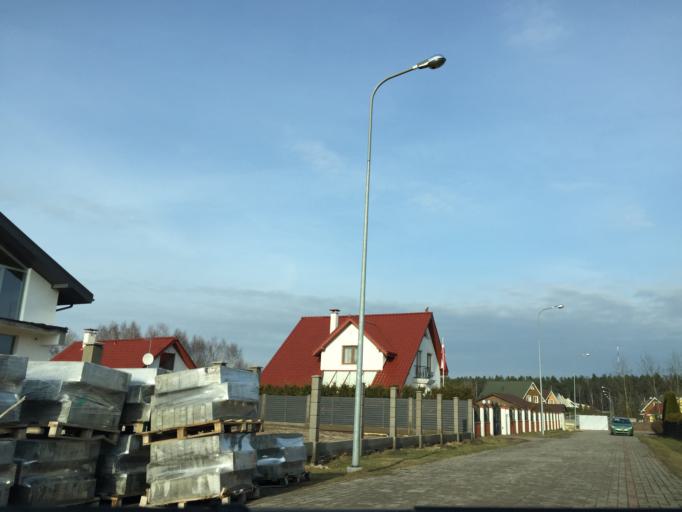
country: LV
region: Stopini
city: Ulbroka
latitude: 56.9258
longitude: 24.2592
